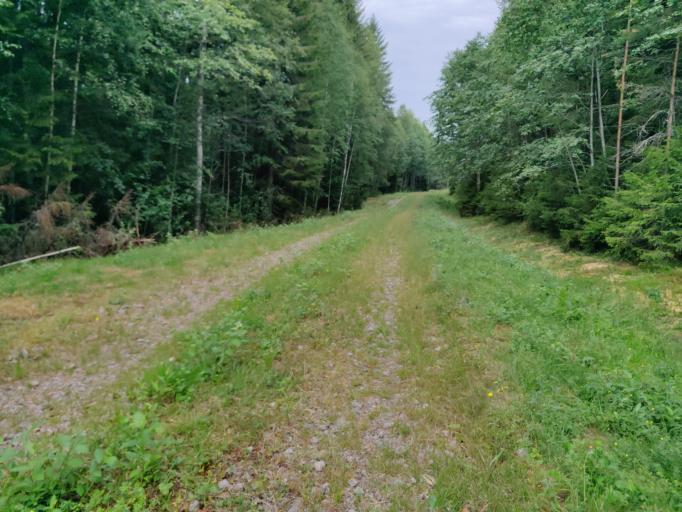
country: SE
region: Vaermland
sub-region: Hagfors Kommun
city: Hagfors
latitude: 59.9642
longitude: 13.5730
